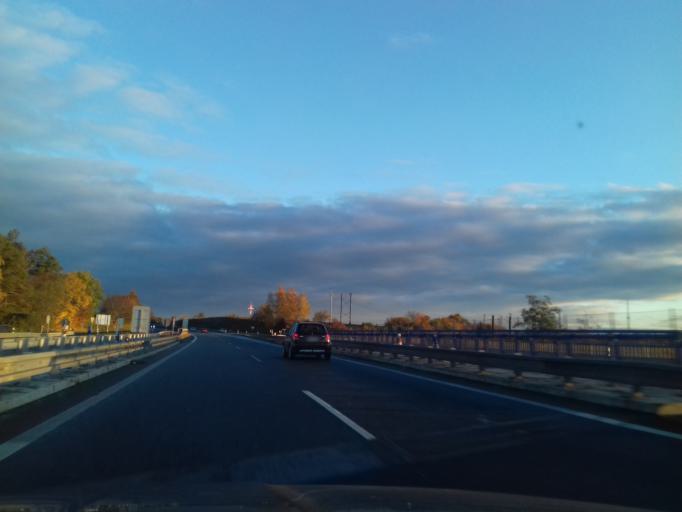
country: CZ
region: Olomoucky
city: Otaslavice
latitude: 49.3695
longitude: 17.0975
